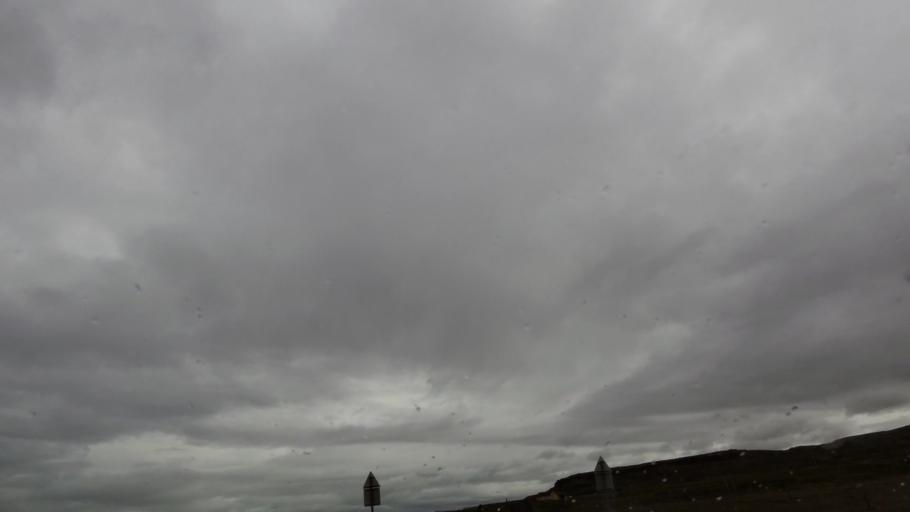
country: IS
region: West
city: Borgarnes
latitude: 65.0244
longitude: -22.1067
